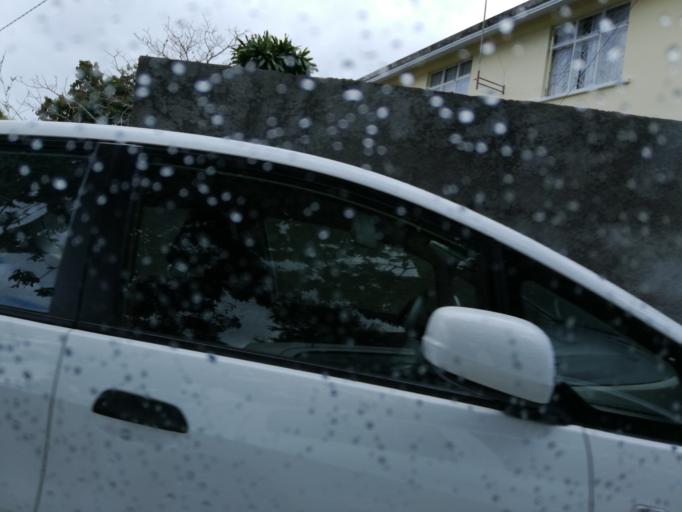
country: MU
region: Moka
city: Moka
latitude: -20.2170
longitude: 57.4723
